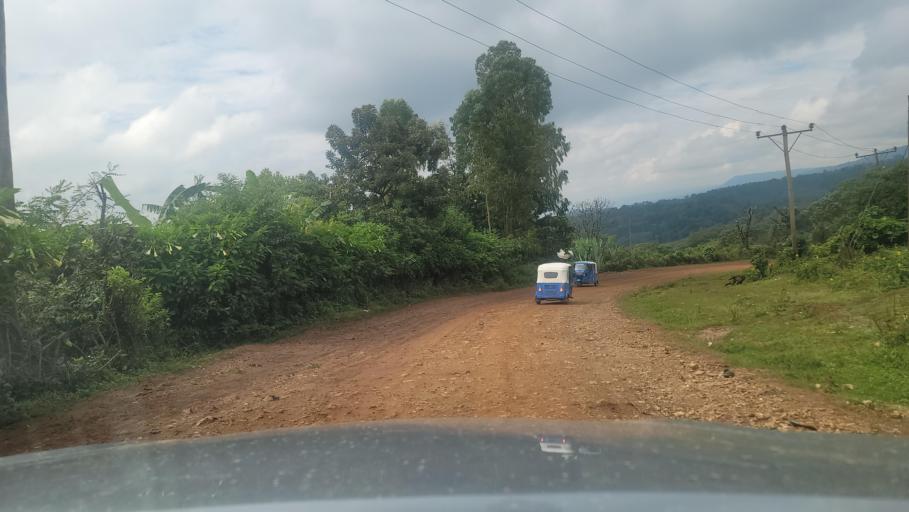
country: ET
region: Oromiya
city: Agaro
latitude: 7.7917
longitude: 36.4409
